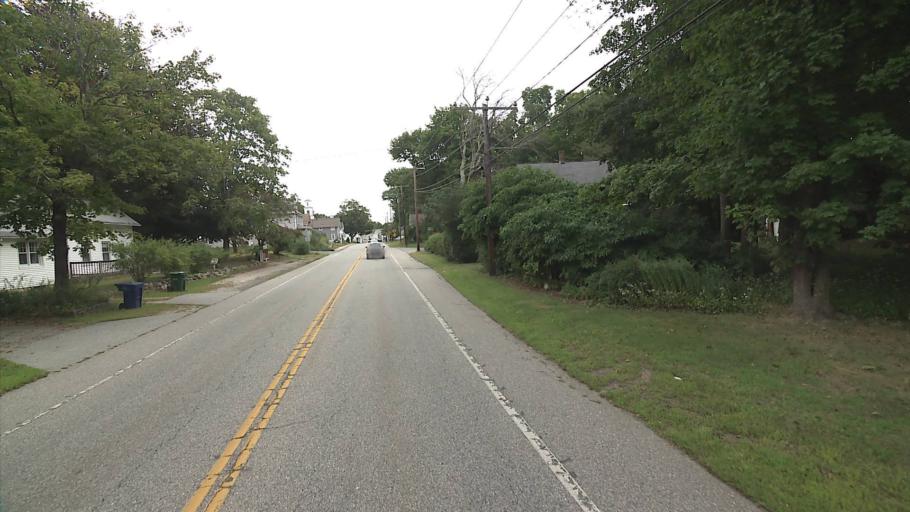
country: US
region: Connecticut
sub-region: New London County
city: Central Waterford
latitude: 41.3388
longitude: -72.1451
